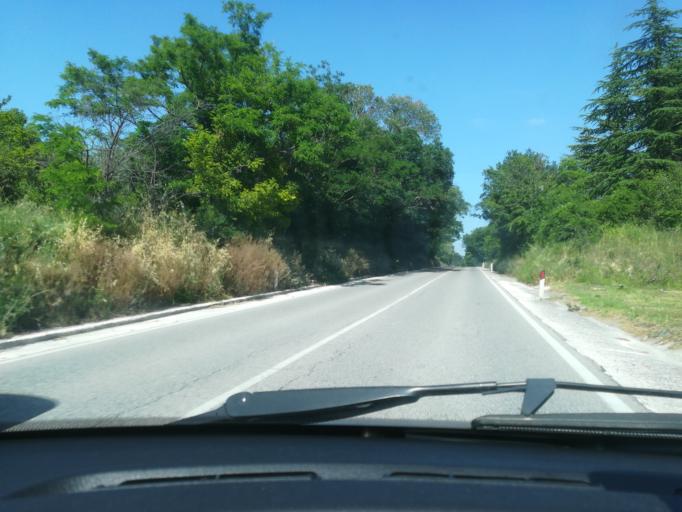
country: IT
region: The Marches
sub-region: Provincia di Macerata
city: Passo di Treia
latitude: 43.2845
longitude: 13.3449
